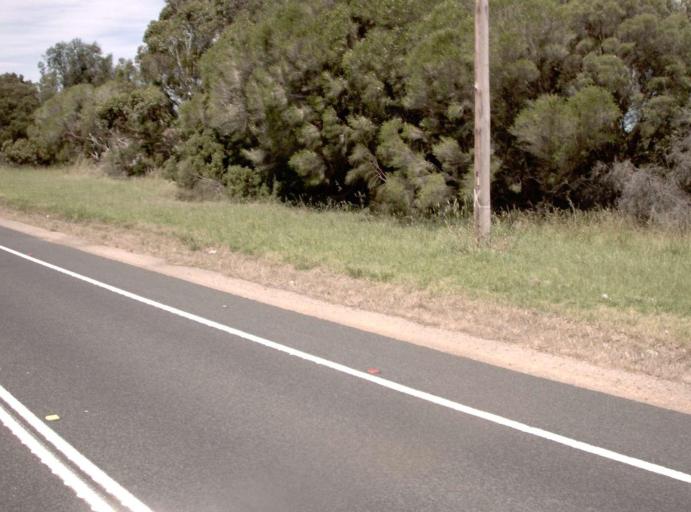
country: AU
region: Victoria
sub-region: Wellington
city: Heyfield
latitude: -38.1076
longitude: 146.8963
